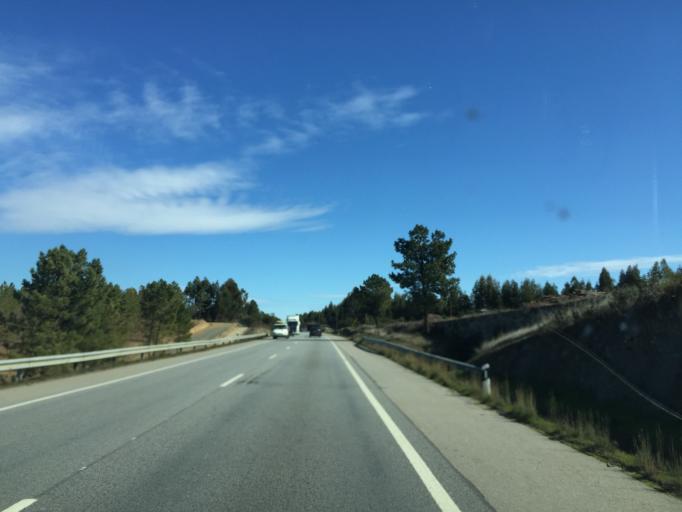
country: PT
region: Castelo Branco
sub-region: Castelo Branco
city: Castelo Branco
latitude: 39.7942
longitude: -7.5456
